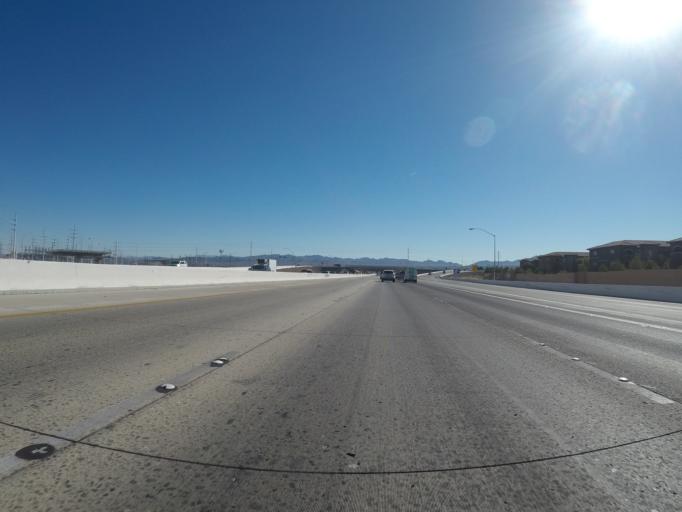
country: US
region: Nevada
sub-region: Clark County
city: Whitney
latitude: 36.0855
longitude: -115.0542
